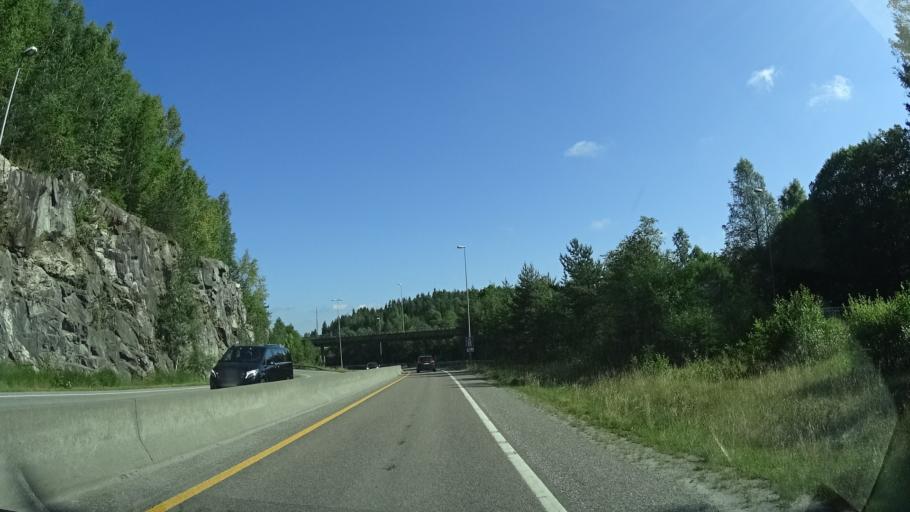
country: NO
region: Akershus
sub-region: Ski
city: Ski
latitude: 59.7390
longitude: 10.7826
